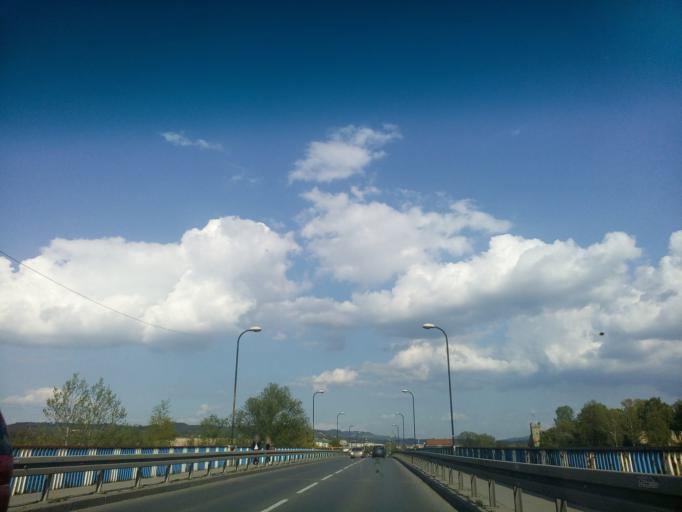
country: PL
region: Lesser Poland Voivodeship
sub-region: Powiat nowosadecki
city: Nowy Sacz
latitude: 49.6296
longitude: 20.6844
